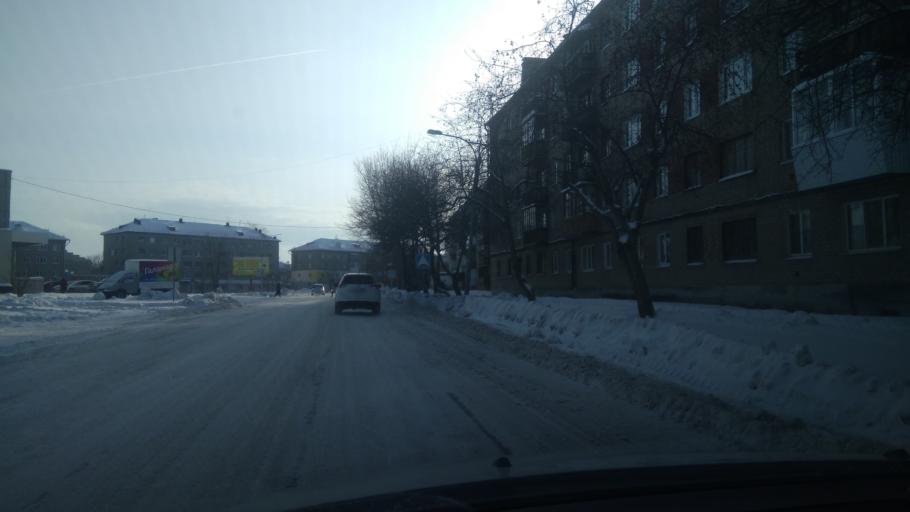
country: RU
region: Sverdlovsk
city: Sukhoy Log
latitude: 56.9099
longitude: 62.0330
